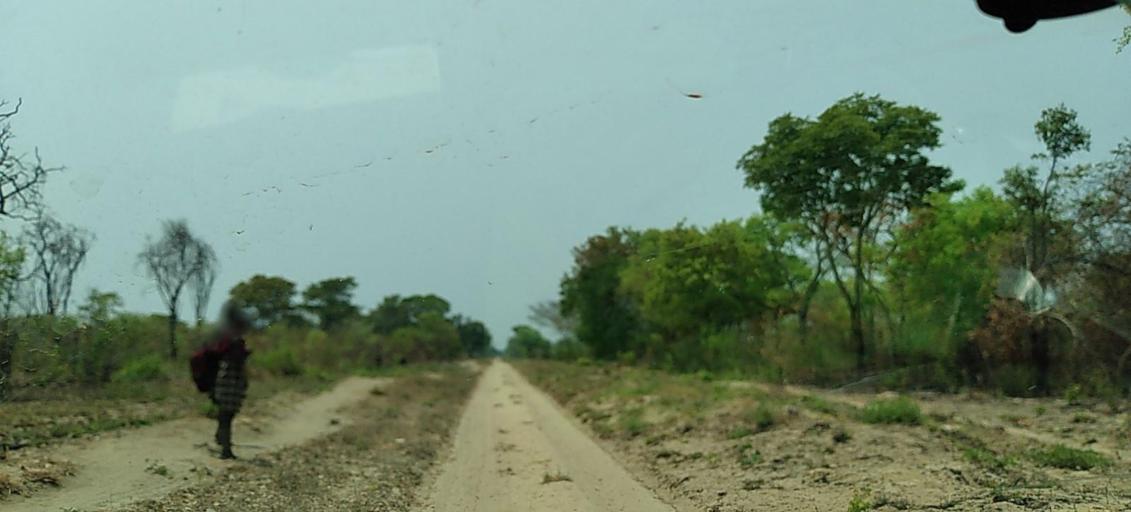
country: ZM
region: Western
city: Lukulu
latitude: -14.1484
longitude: 23.2928
